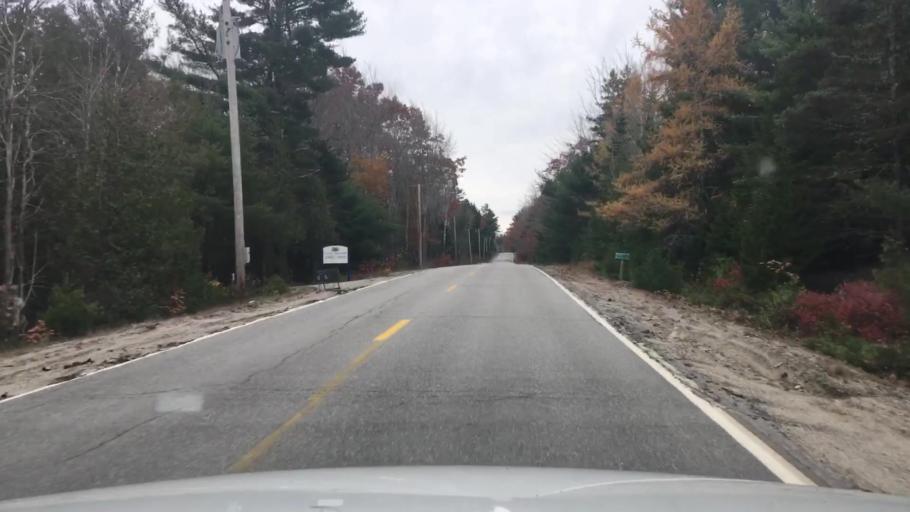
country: US
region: Maine
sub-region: Hancock County
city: Sedgwick
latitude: 44.3129
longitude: -68.5707
